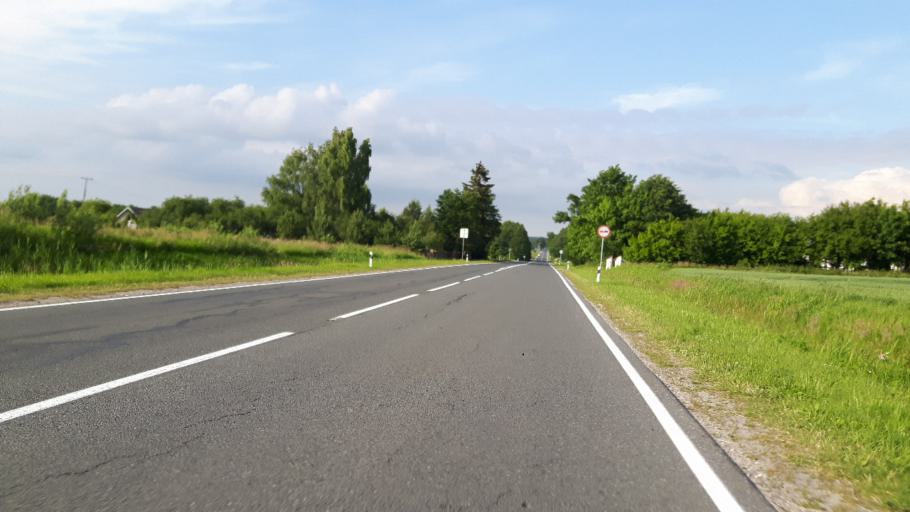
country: RU
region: Kaliningrad
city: Ladushkin
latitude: 54.5414
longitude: 20.1399
